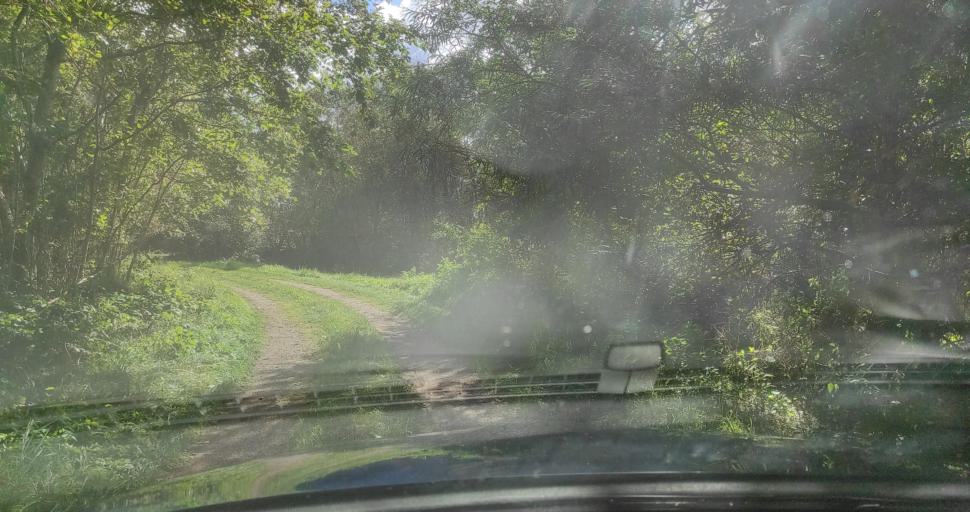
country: LV
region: Ventspils Rajons
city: Piltene
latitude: 57.2695
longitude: 21.6024
